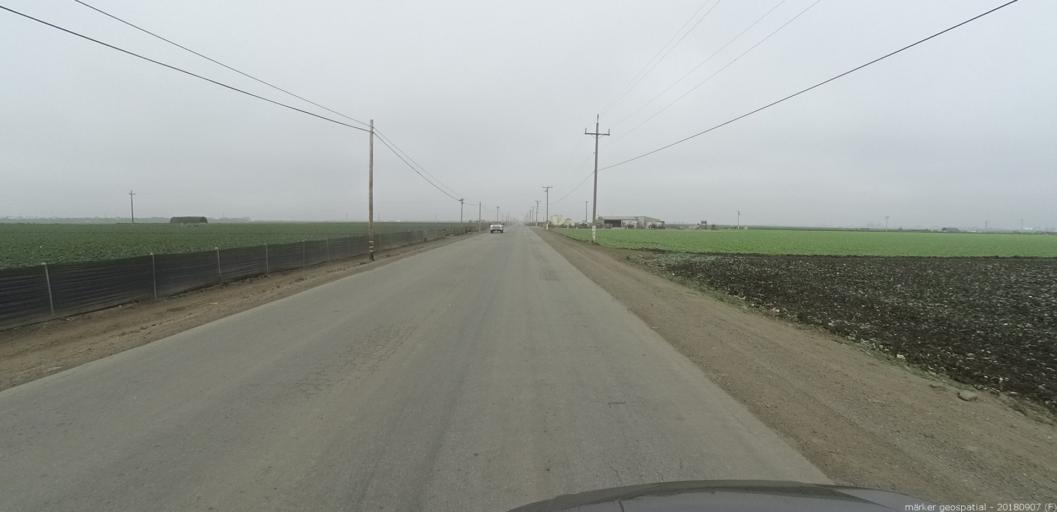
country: US
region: California
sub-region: Monterey County
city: Castroville
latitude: 36.7268
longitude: -121.7496
